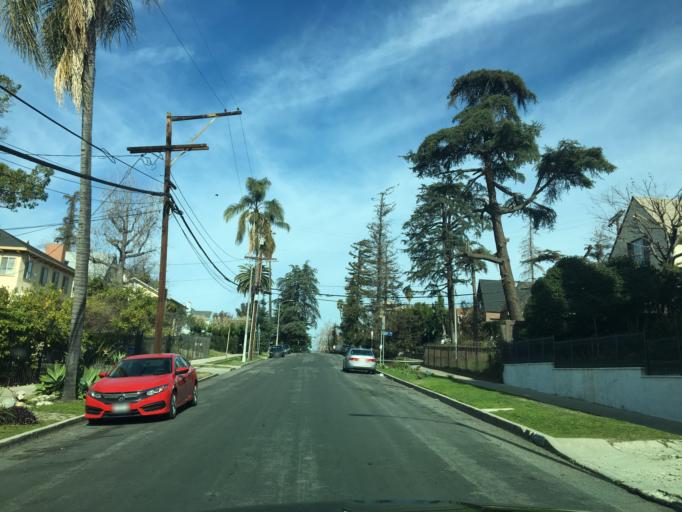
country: US
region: California
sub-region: Los Angeles County
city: Silver Lake
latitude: 34.0672
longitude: -118.2880
